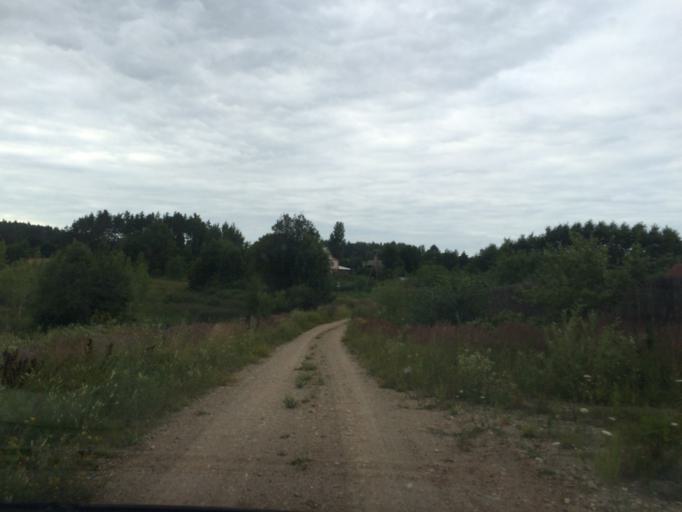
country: LV
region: Rezekne
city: Rezekne
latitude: 56.5876
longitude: 27.4109
